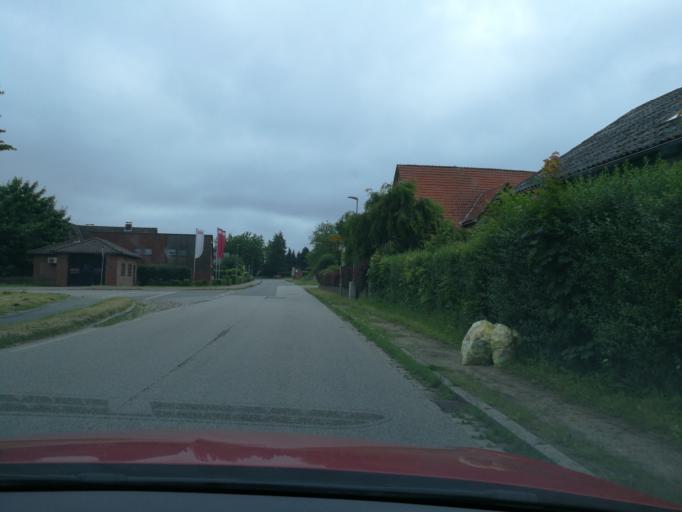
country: DE
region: Schleswig-Holstein
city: Lasbek
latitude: 53.7436
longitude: 10.3741
